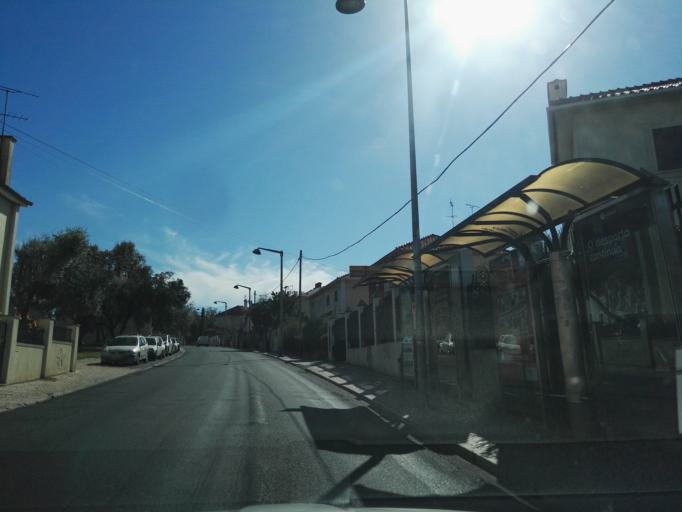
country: PT
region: Lisbon
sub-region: Loures
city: Moscavide
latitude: 38.7764
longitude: -9.1180
